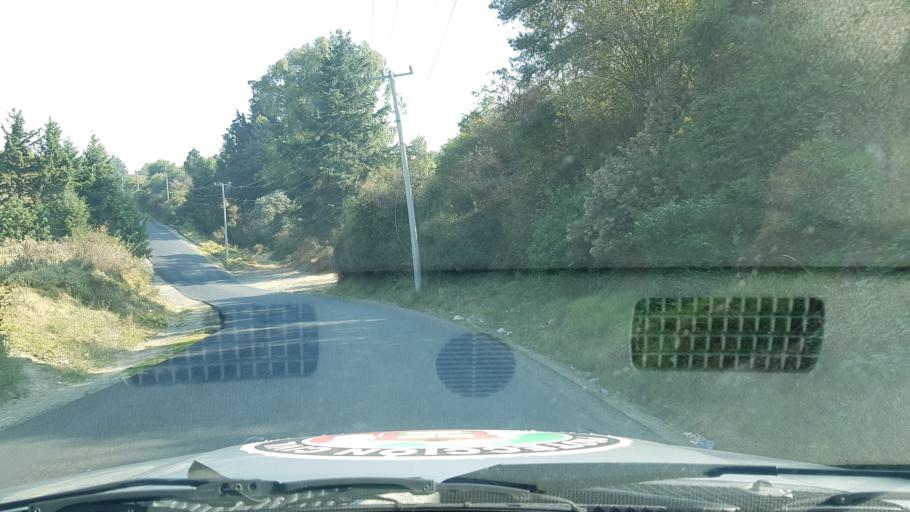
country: MX
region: Mexico
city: Atlautla
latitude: 19.0389
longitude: -98.7740
